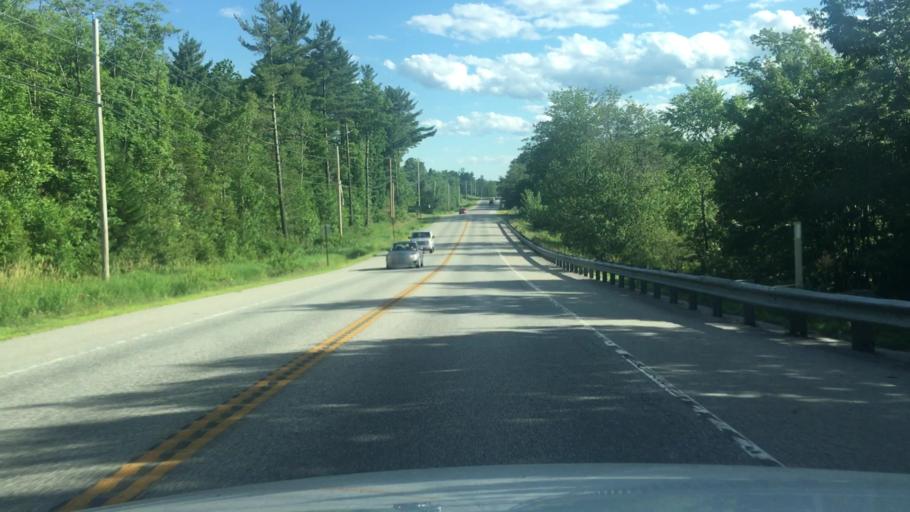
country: US
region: Maine
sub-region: Androscoggin County
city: Livermore
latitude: 44.4110
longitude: -70.2228
